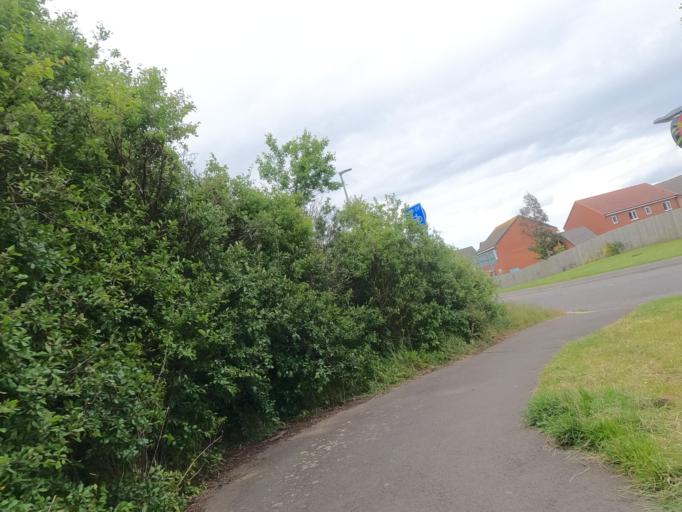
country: GB
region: England
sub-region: Northumberland
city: Seaton Delaval
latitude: 55.1047
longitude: -1.5414
